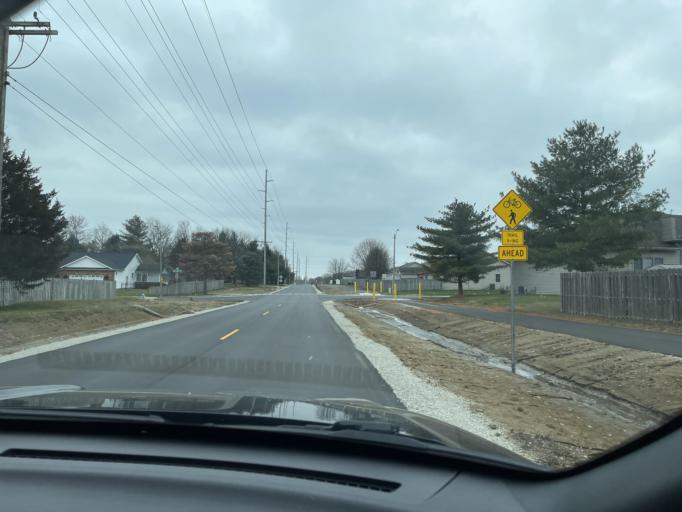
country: US
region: Illinois
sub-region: Sangamon County
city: Rochester
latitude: 39.7593
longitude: -89.5787
